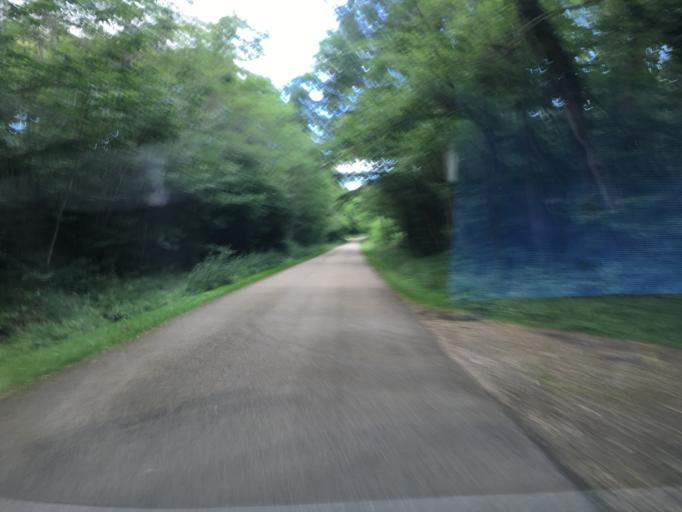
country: FR
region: Bourgogne
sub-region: Departement de l'Yonne
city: Fleury-la-Vallee
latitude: 47.8642
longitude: 3.4814
